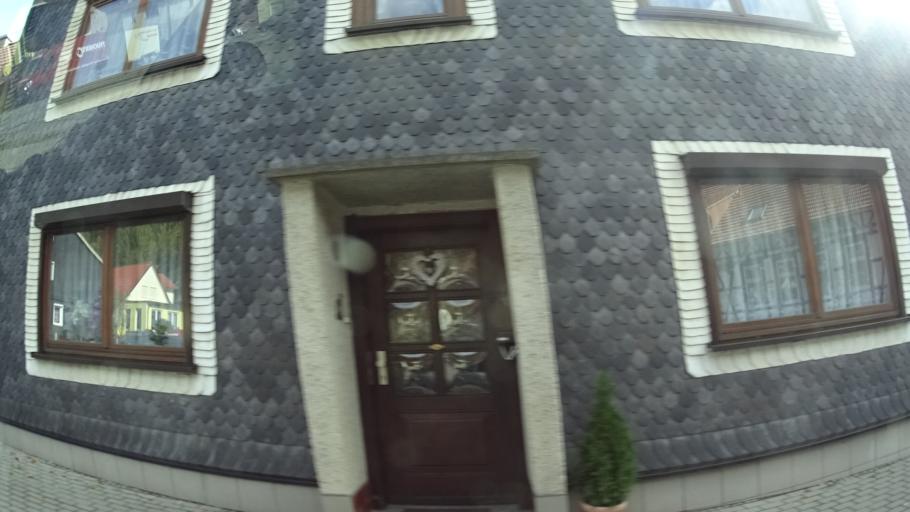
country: DE
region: Thuringia
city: Unterschonau
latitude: 50.7121
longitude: 10.5739
